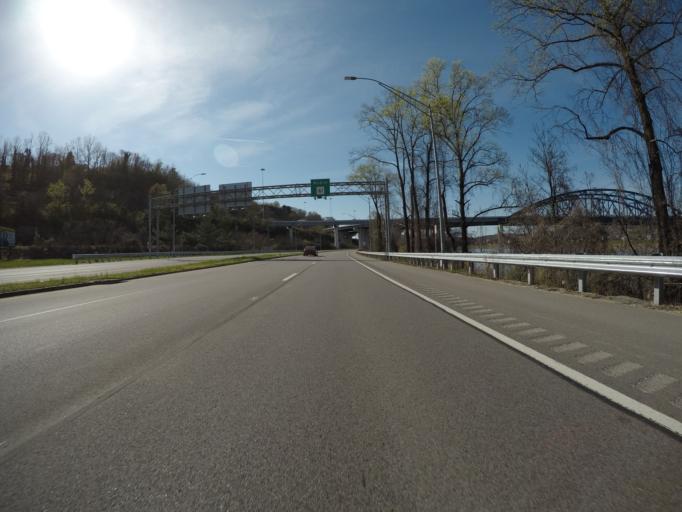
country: US
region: West Virginia
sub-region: Kanawha County
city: Charleston
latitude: 38.3531
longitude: -81.6477
